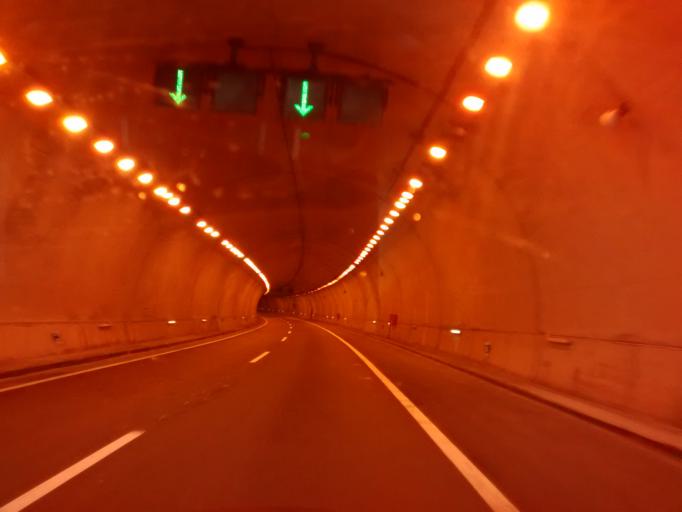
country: ES
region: Cantabria
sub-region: Provincia de Cantabria
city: Pesquera
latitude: 43.0887
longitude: -4.0794
